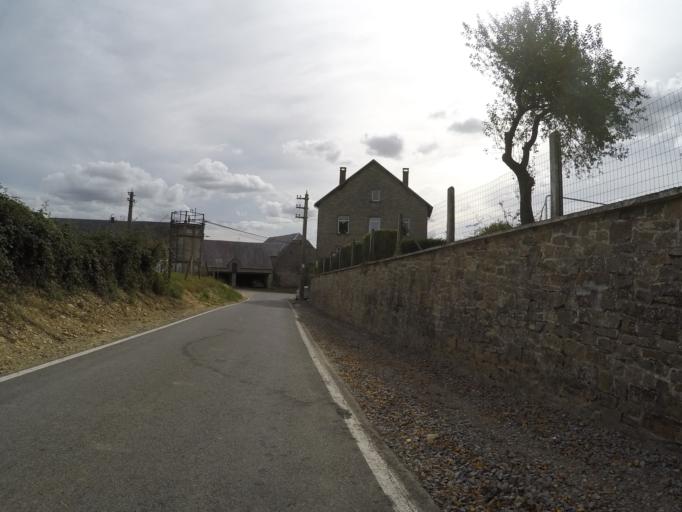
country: BE
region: Wallonia
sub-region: Province de Namur
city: Assesse
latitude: 50.3173
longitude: 4.9773
